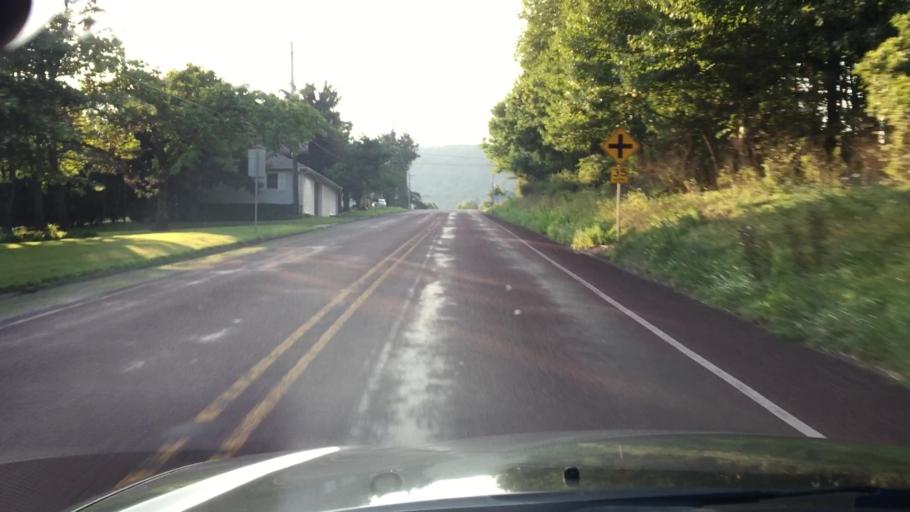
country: US
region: Pennsylvania
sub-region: Carbon County
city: Weatherly
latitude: 40.9228
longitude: -75.8634
